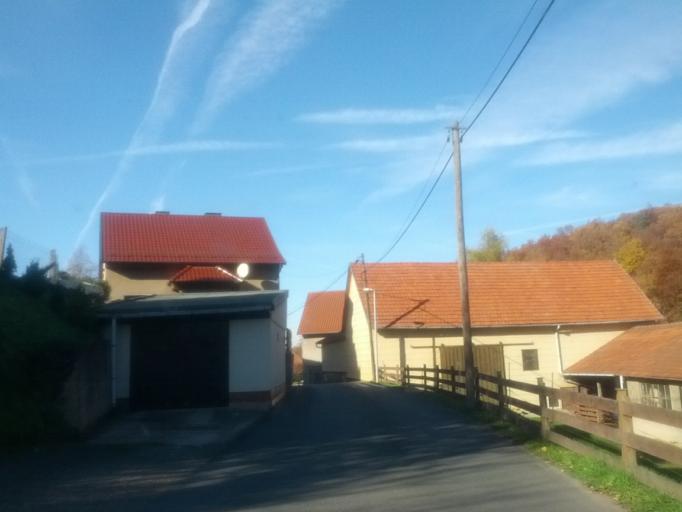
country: DE
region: Thuringia
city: Seebach
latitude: 50.9316
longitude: 10.4350
